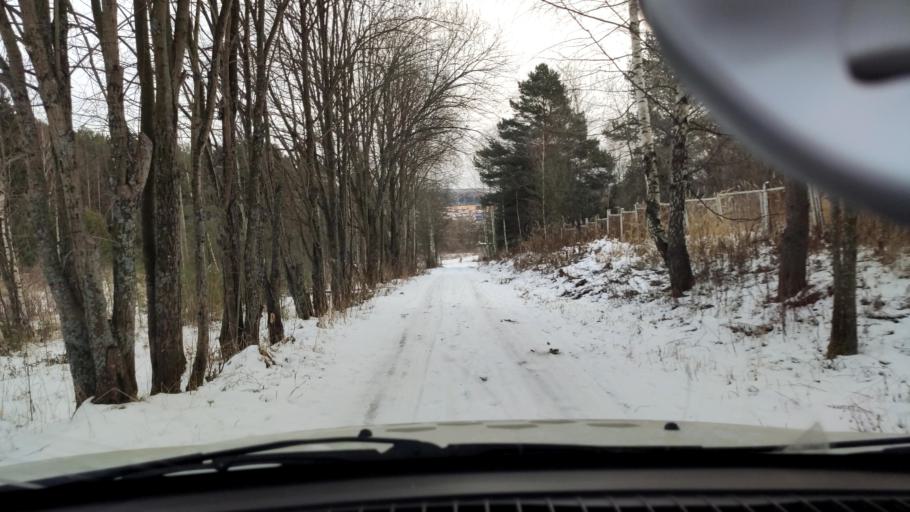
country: RU
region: Perm
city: Lobanovo
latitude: 57.8266
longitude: 56.3472
